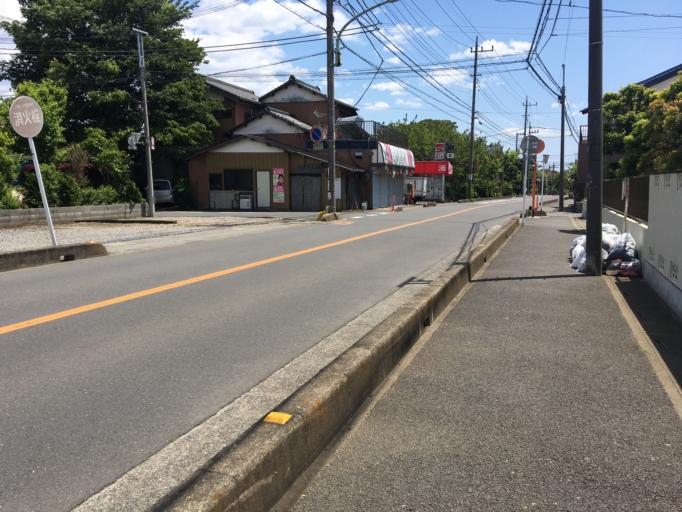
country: JP
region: Saitama
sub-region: Kawaguchi-shi
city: Hatogaya-honcho
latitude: 35.8461
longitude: 139.7534
